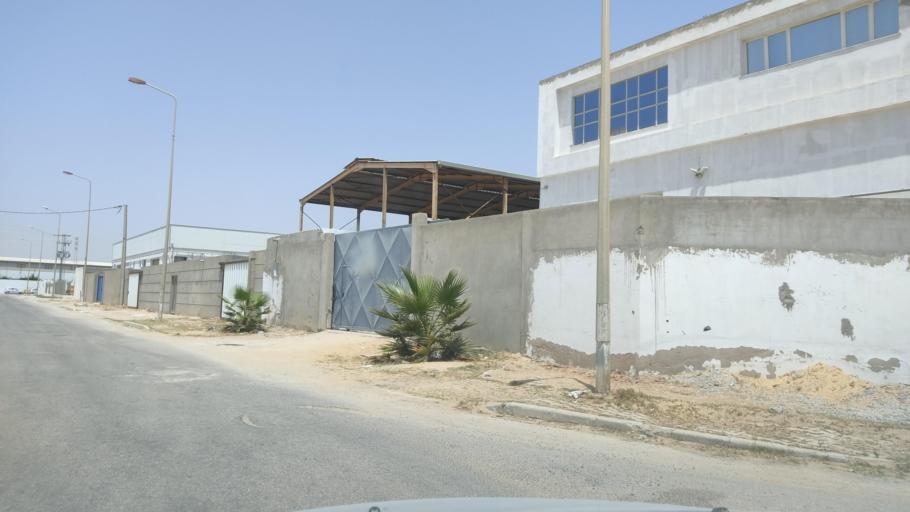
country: TN
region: Safaqis
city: Sfax
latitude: 34.6637
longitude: 10.6978
